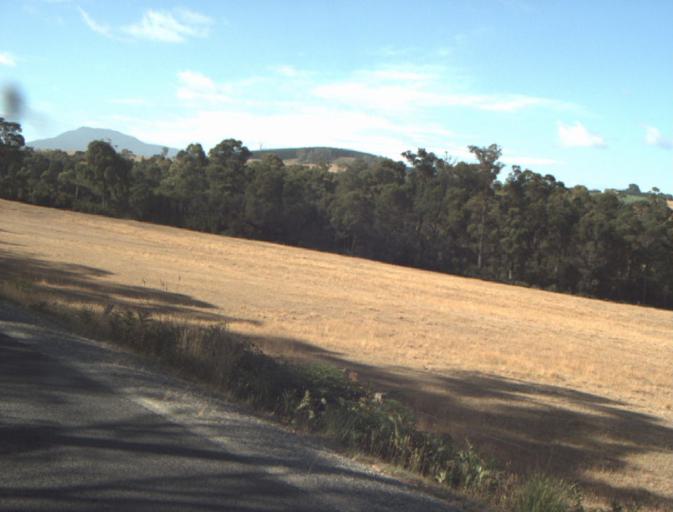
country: AU
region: Tasmania
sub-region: Dorset
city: Bridport
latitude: -41.1489
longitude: 147.2337
